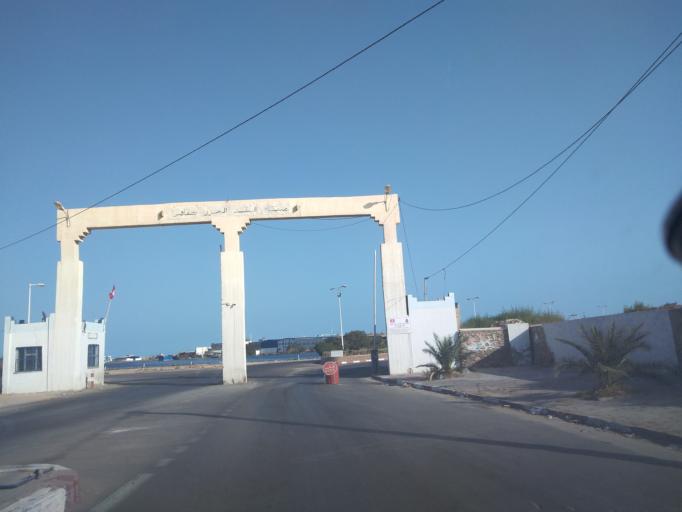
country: TN
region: Safaqis
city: Sfax
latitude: 34.7218
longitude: 10.7603
